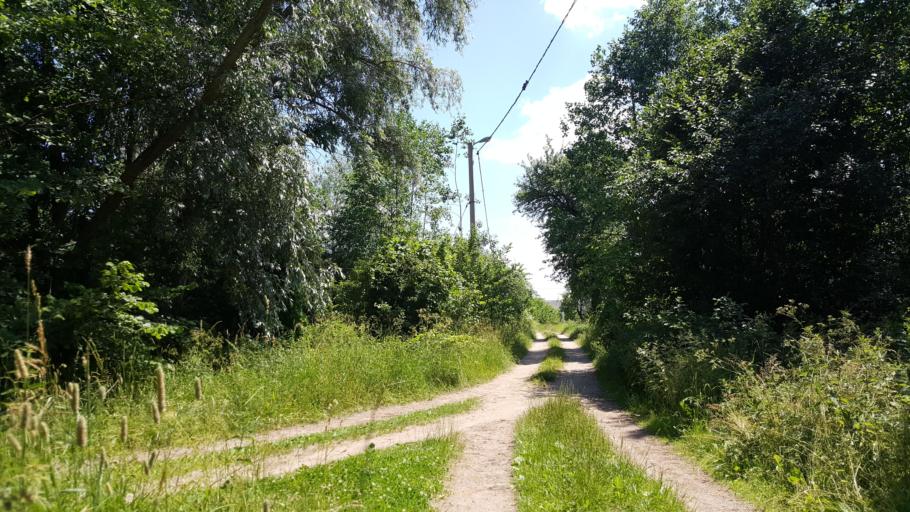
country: BY
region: Brest
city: Kamyanyets
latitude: 52.4123
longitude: 23.8277
